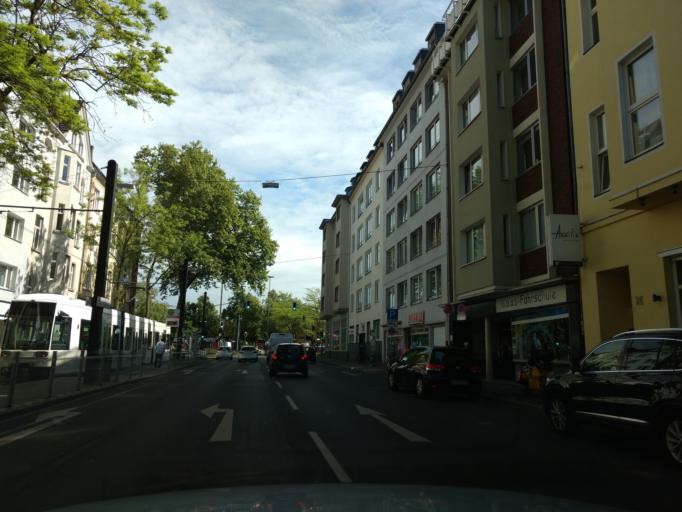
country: DE
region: North Rhine-Westphalia
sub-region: Regierungsbezirk Dusseldorf
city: Dusseldorf
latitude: 51.2376
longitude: 6.8020
